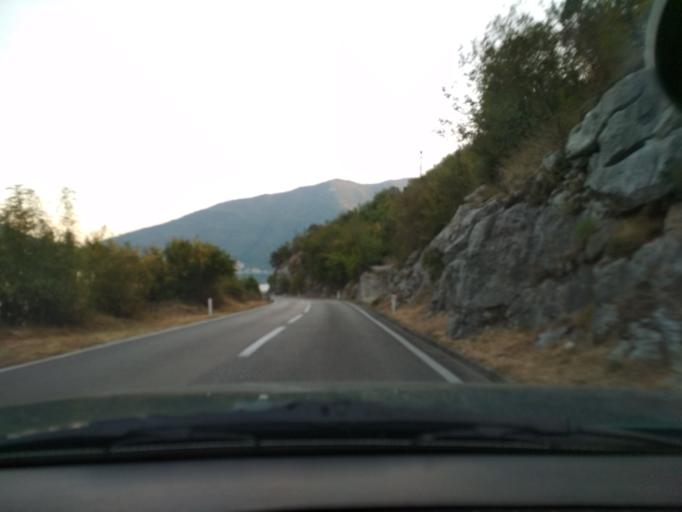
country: ME
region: Kotor
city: Risan
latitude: 42.5074
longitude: 18.6770
